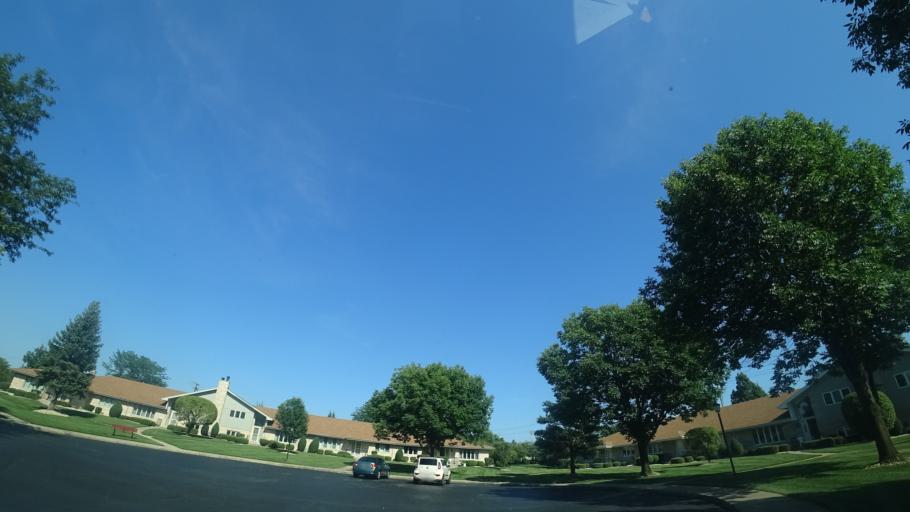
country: US
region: Illinois
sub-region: Will County
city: Mokena
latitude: 41.5651
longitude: -87.8819
